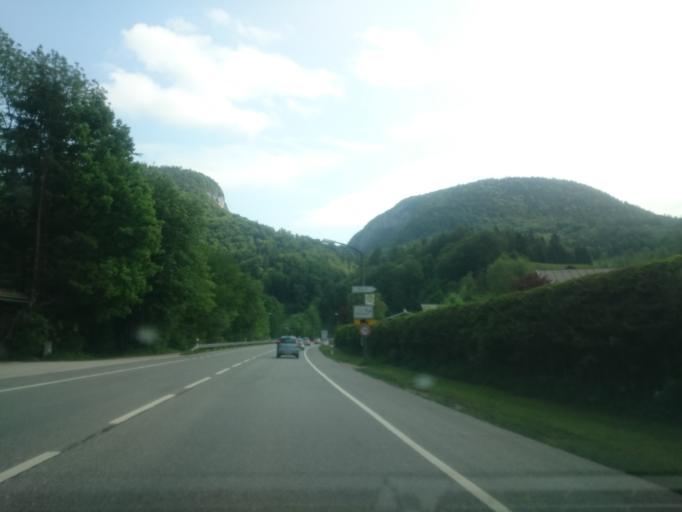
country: DE
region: Bavaria
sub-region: Upper Bavaria
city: Berchtesgaden
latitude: 47.6523
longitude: 13.0379
